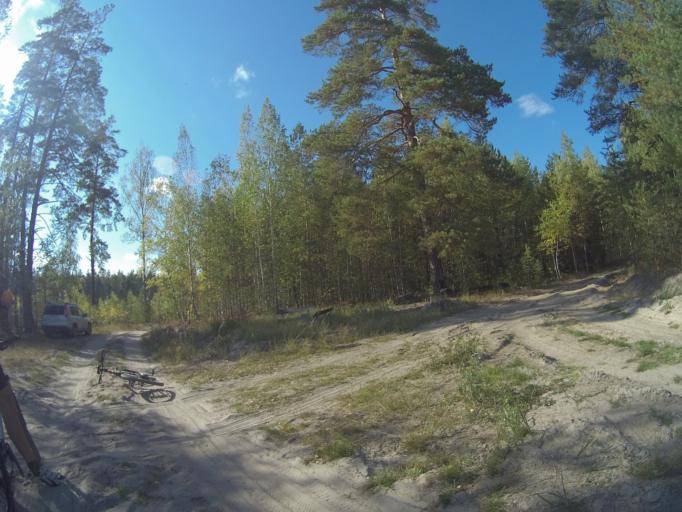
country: RU
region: Vladimir
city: Vorsha
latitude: 55.8881
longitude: 40.1743
